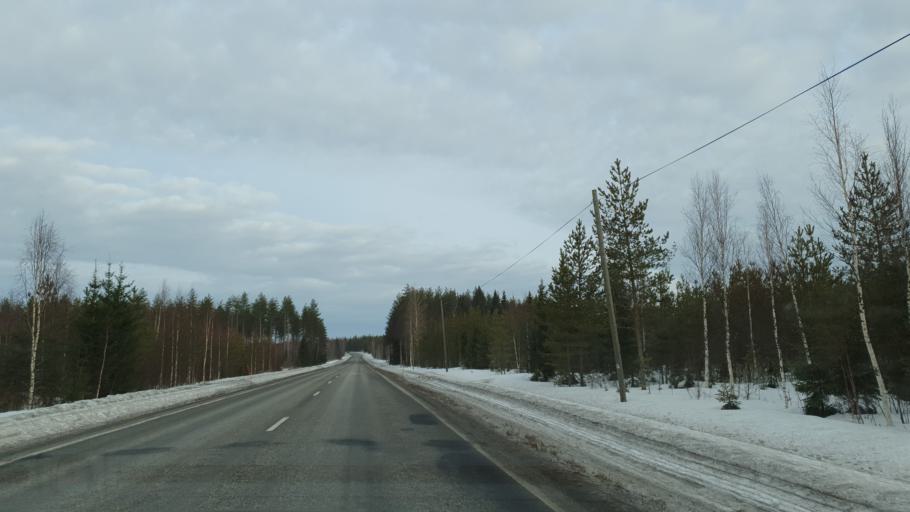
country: FI
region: Kainuu
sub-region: Kajaani
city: Vuokatti
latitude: 64.1932
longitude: 28.1751
